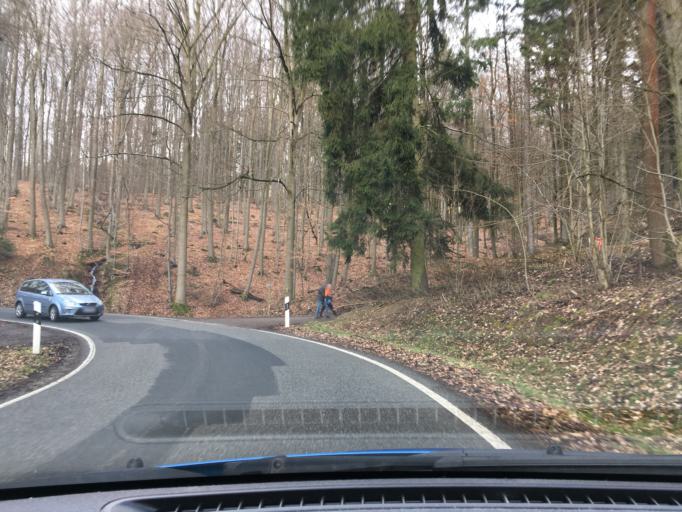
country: DE
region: Lower Saxony
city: Buhren
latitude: 51.4981
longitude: 9.6356
